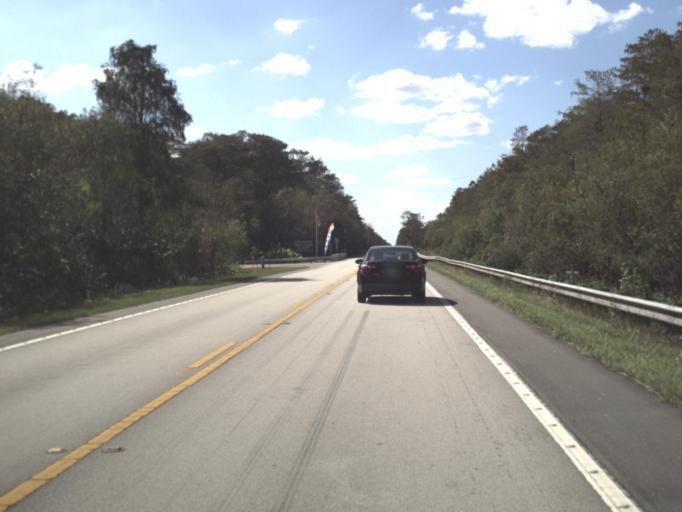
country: US
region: Florida
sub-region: Miami-Dade County
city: Kendall West
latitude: 25.8554
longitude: -81.0187
